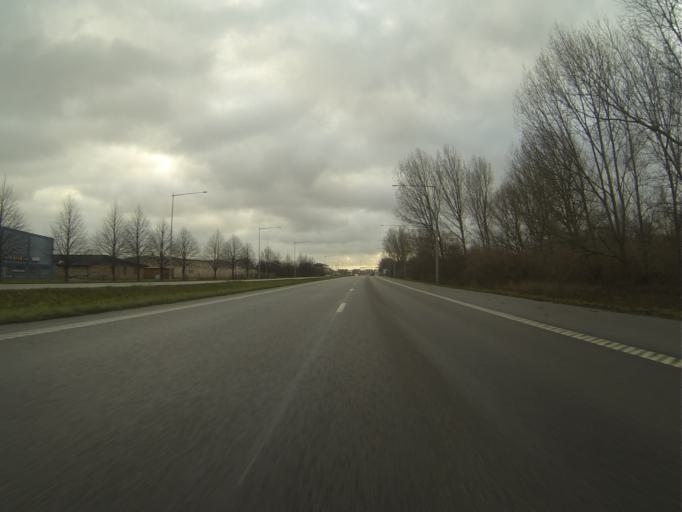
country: SE
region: Skane
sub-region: Burlovs Kommun
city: Arloev
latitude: 55.6361
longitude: 13.0567
